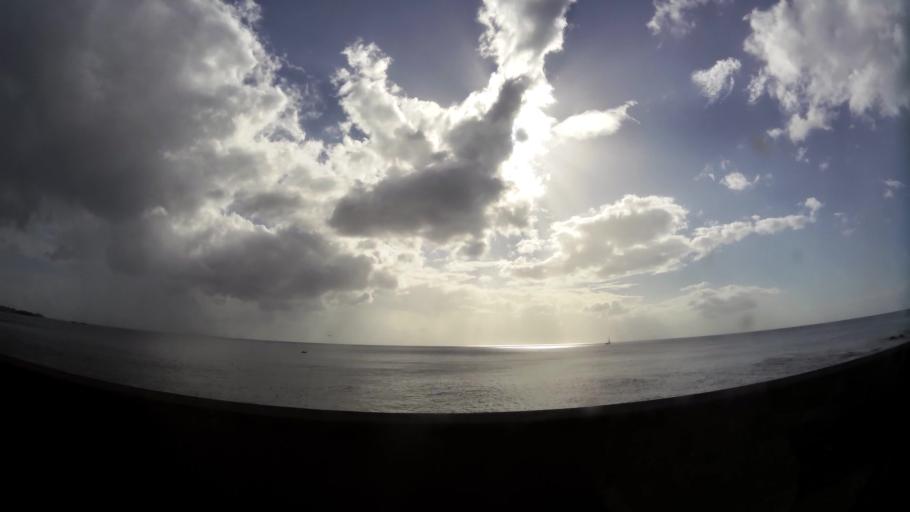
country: DM
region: Saint George
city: Roseau
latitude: 15.3199
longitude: -61.3939
